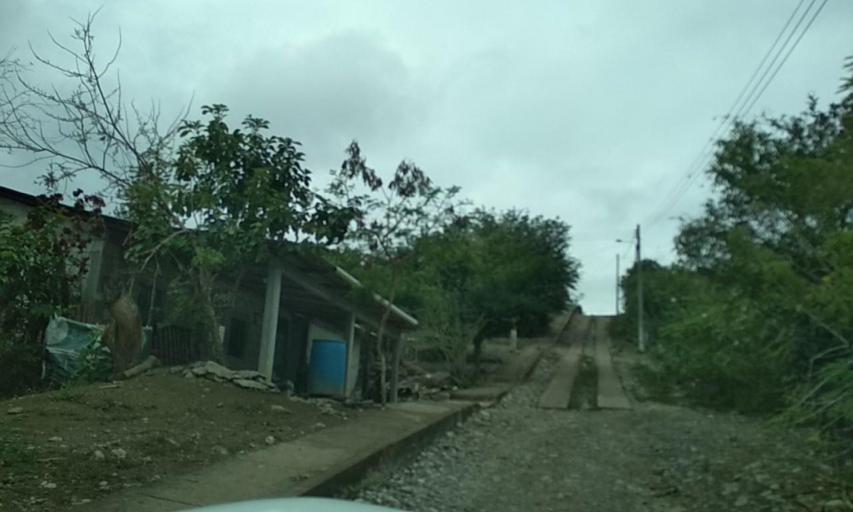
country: MX
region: Veracruz
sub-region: Coatzintla
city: Manuel Maria Contreras
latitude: 20.3411
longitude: -97.4652
